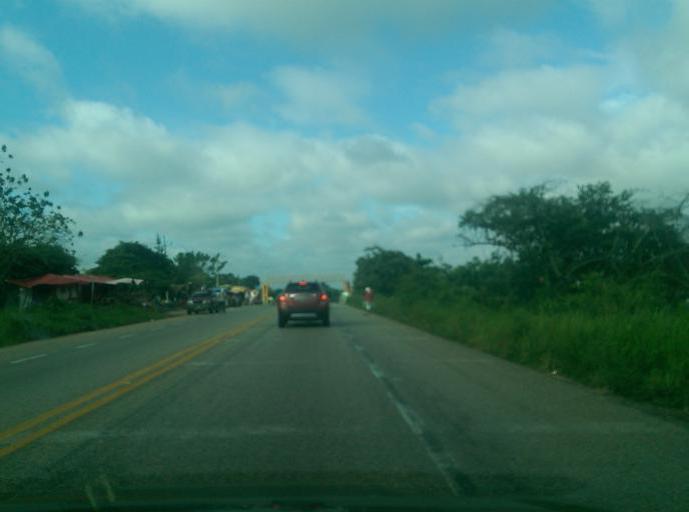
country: MX
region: Tabasco
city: Aquiles Serdan
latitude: 17.6994
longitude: -92.2580
